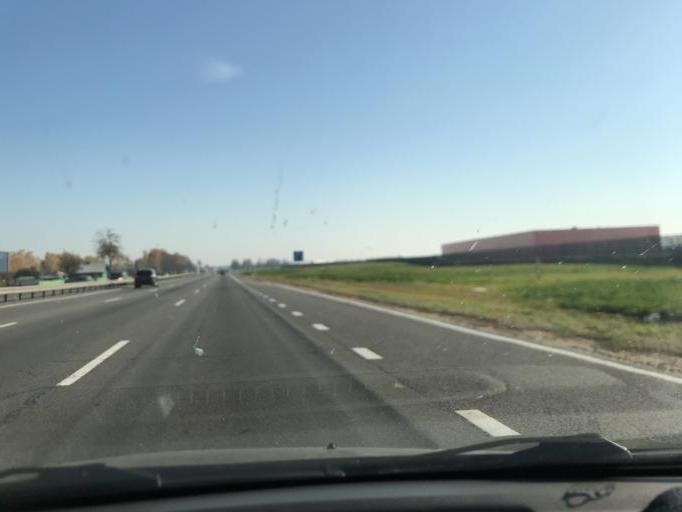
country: BY
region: Minsk
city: Pryvol'ny
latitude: 53.8110
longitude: 27.7805
